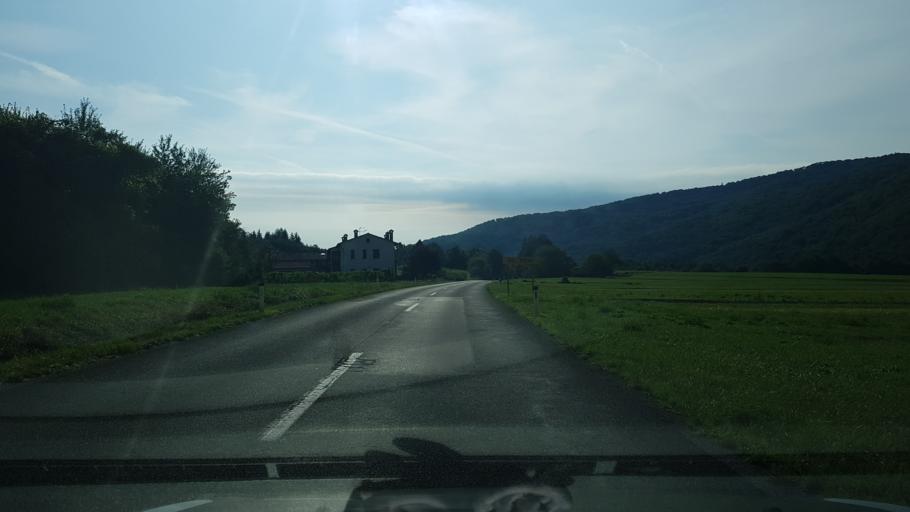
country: SI
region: Divaca
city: Divaca
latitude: 45.6551
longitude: 14.0413
